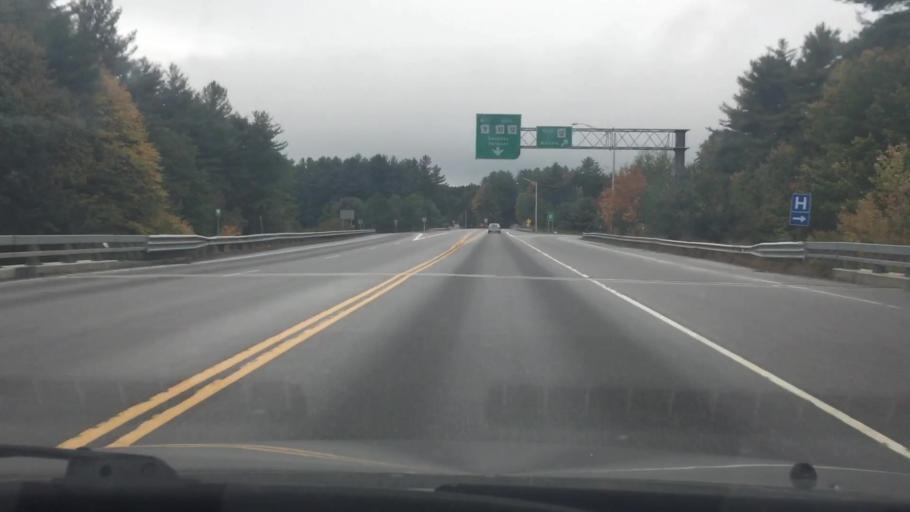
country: US
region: New Hampshire
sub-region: Cheshire County
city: Keene
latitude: 42.9455
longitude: -72.2923
